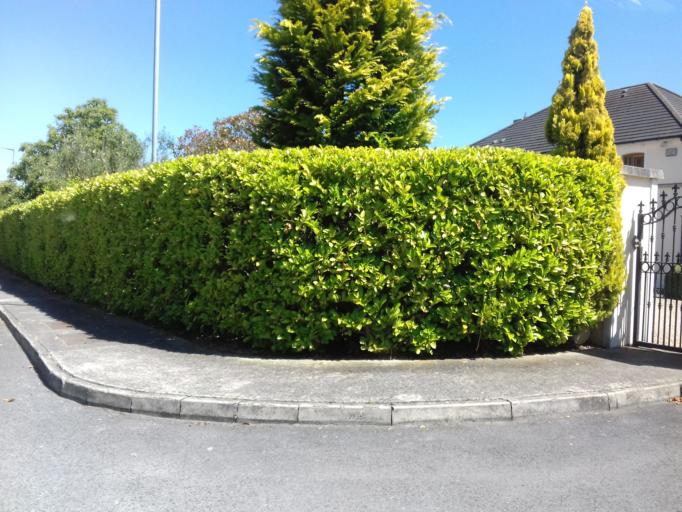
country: IE
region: Leinster
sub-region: Fingal County
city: Swords
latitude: 53.4848
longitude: -6.2712
